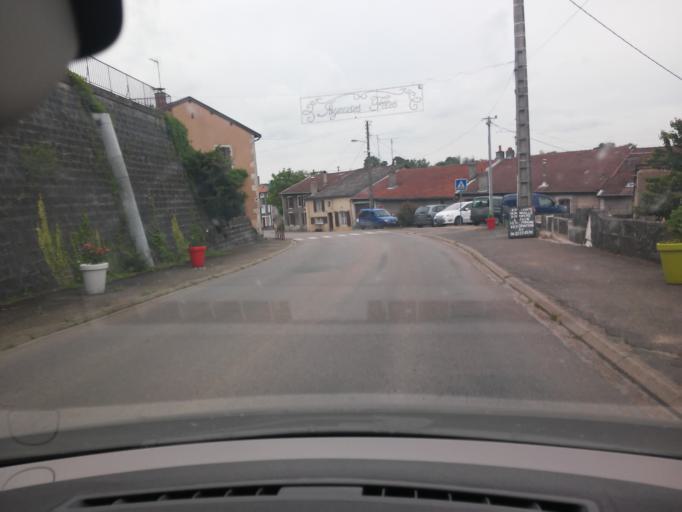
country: FR
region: Lorraine
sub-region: Departement de la Meuse
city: Lerouville
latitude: 48.8020
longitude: 5.5278
